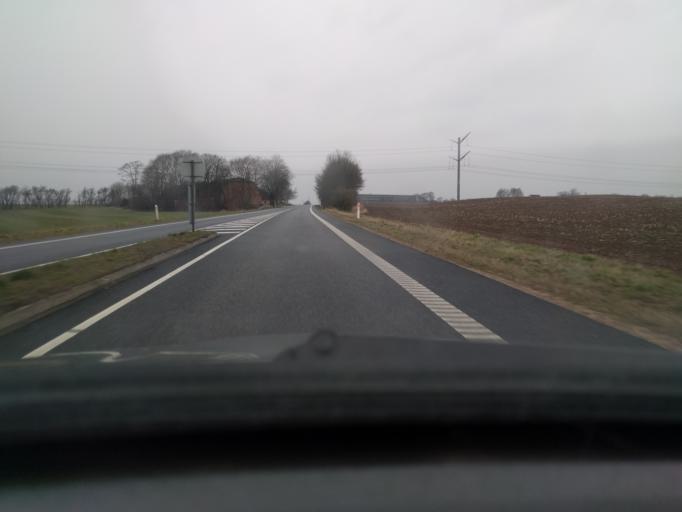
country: DK
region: Central Jutland
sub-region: Silkeborg Kommune
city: Kjellerup
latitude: 56.2509
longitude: 9.4522
